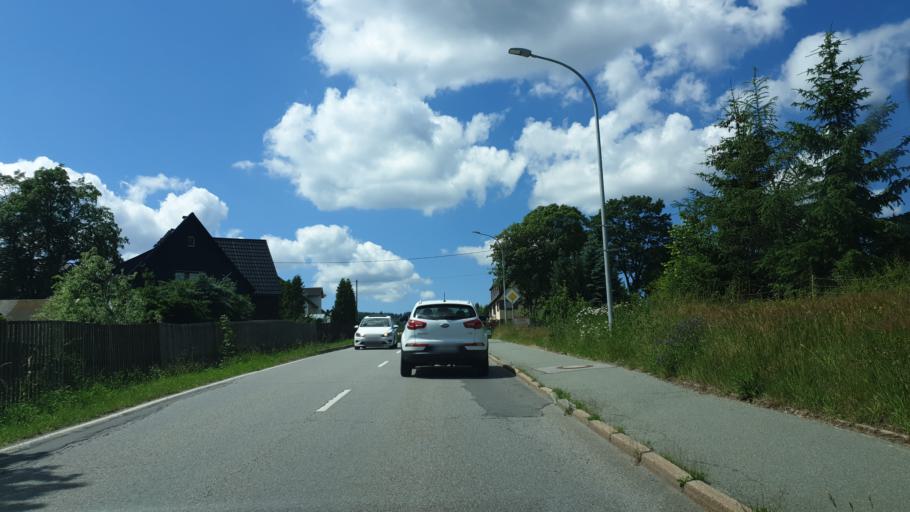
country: DE
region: Saxony
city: Schwarzenberg
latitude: 50.5367
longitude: 12.7758
